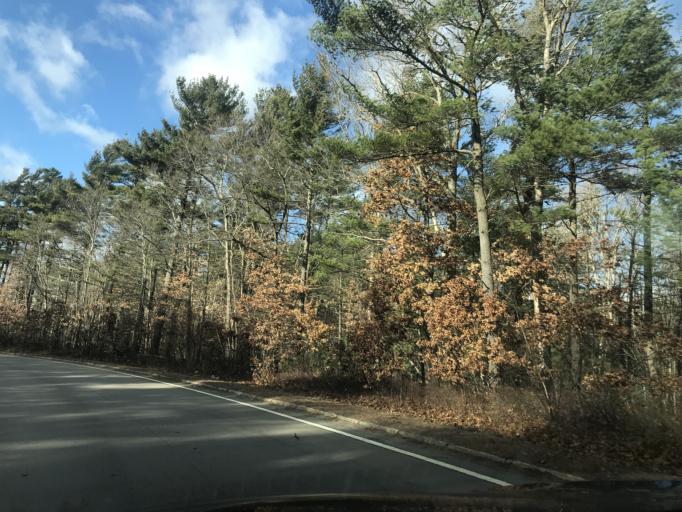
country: US
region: Massachusetts
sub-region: Plymouth County
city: North Pembroke
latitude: 42.1098
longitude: -70.7656
